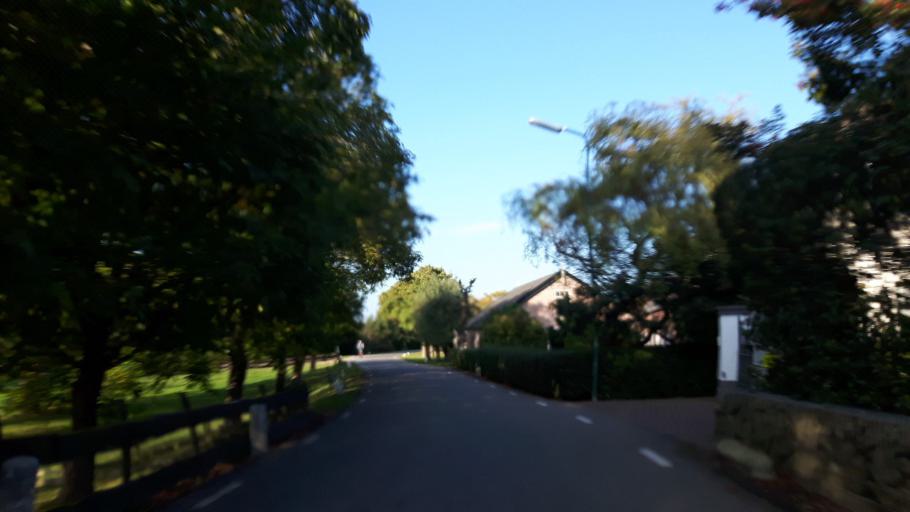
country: NL
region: Utrecht
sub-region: Gemeente Montfoort
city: Montfoort
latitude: 52.0325
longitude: 4.9279
